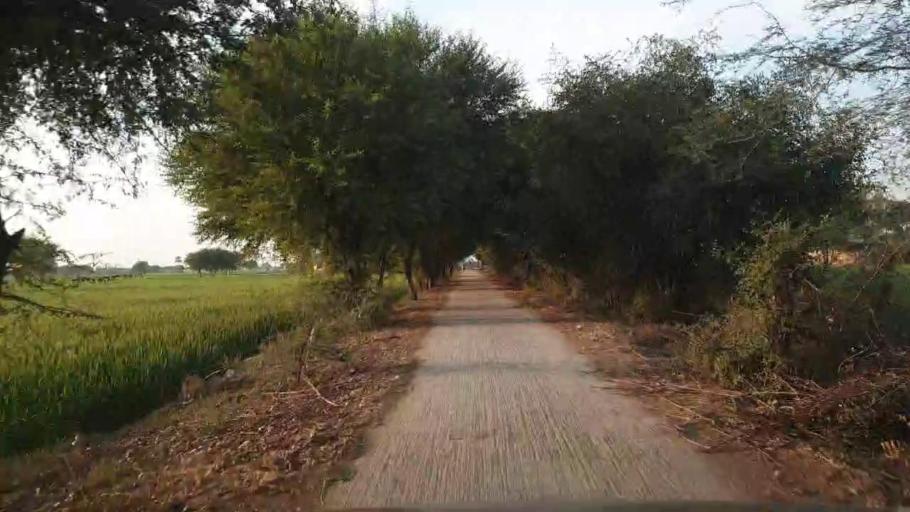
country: PK
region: Sindh
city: Shahpur Chakar
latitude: 26.1710
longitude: 68.6243
